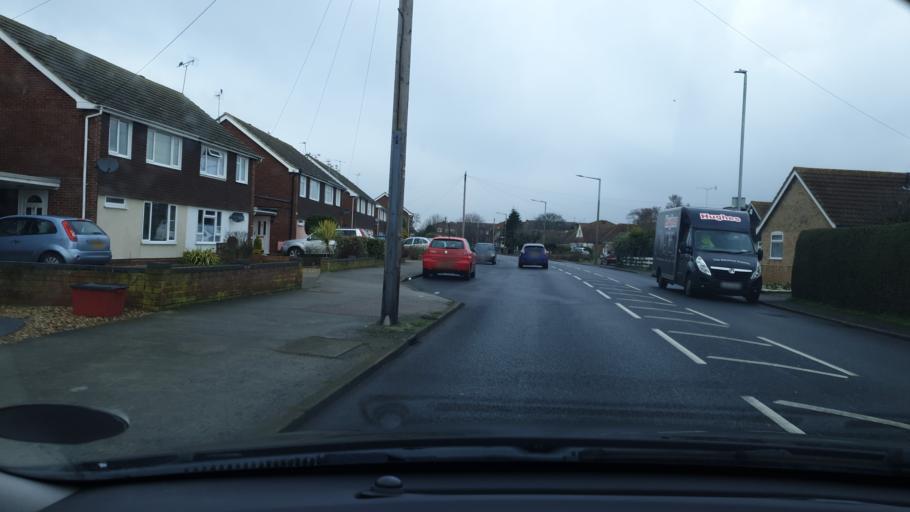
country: GB
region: England
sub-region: Essex
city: Little Clacton
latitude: 51.8007
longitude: 1.1307
